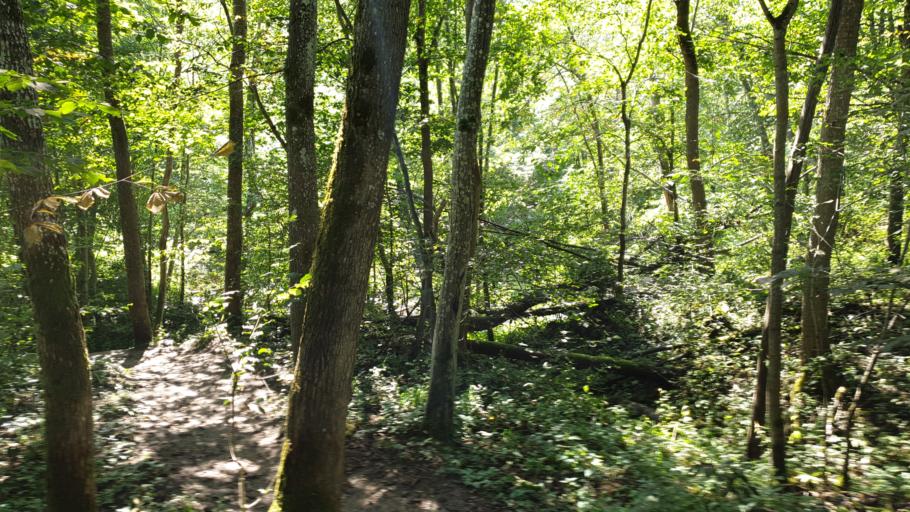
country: LT
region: Vilnius County
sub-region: Vilniaus Rajonas
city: Vievis
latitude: 54.8235
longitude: 24.9393
